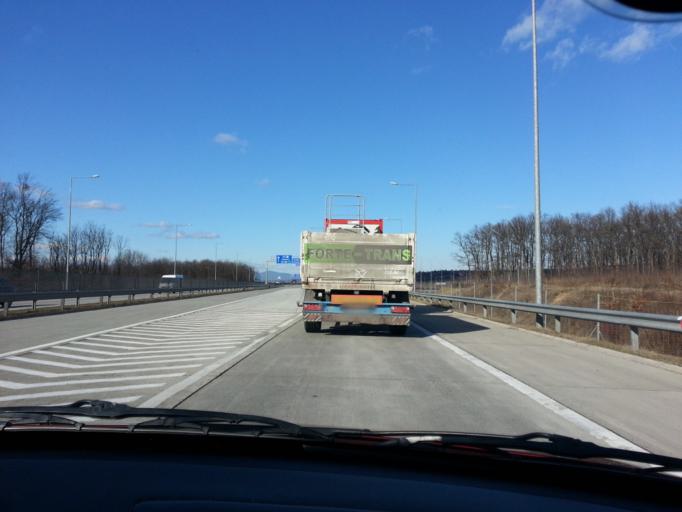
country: HU
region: Pest
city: Szada
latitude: 47.6071
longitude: 19.3195
